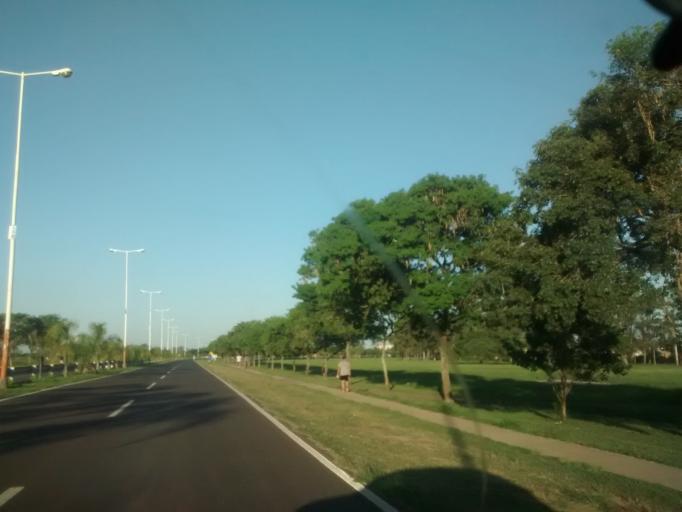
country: AR
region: Chaco
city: Fontana
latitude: -27.4415
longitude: -59.0353
